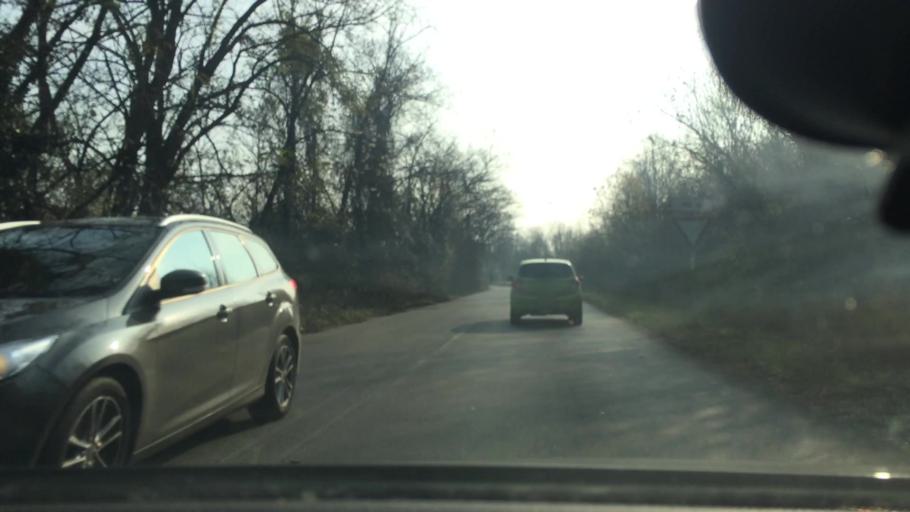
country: IT
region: Lombardy
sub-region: Provincia di Monza e Brianza
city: Villaggio del Sole
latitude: 45.6000
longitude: 9.0973
